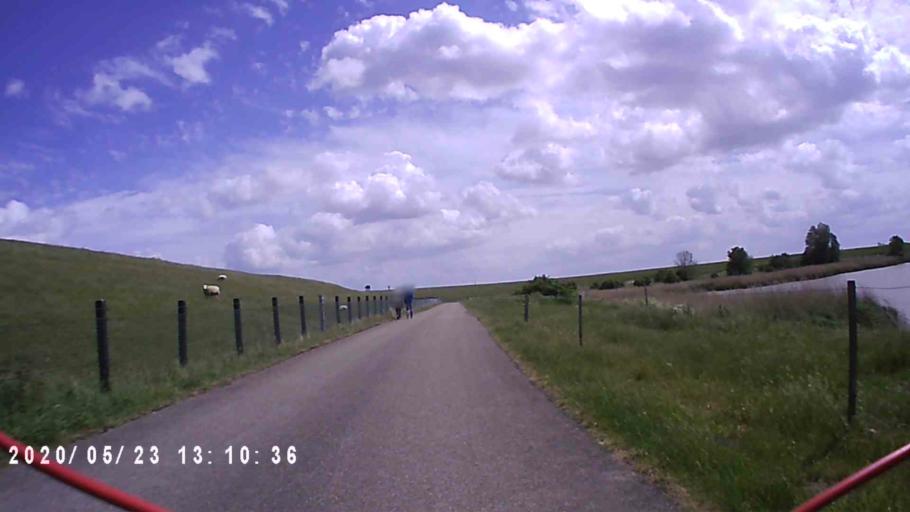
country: DE
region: Lower Saxony
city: Emden
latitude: 53.3012
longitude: 7.0810
